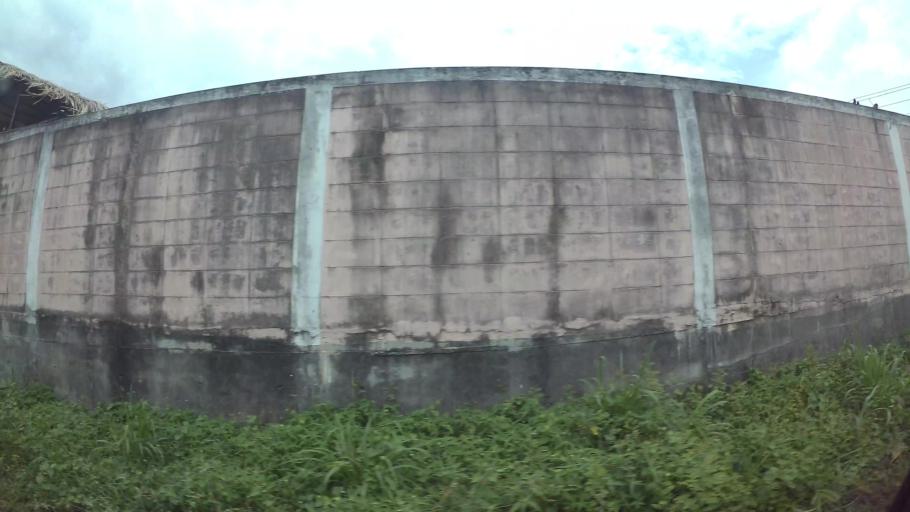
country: TH
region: Chon Buri
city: Si Racha
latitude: 13.1604
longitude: 100.9777
